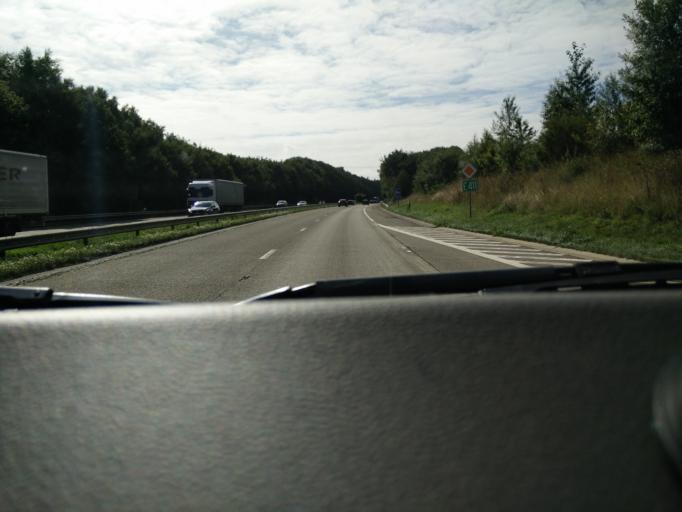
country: BE
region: Wallonia
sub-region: Province de Namur
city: Ciney
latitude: 50.2546
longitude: 5.0479
